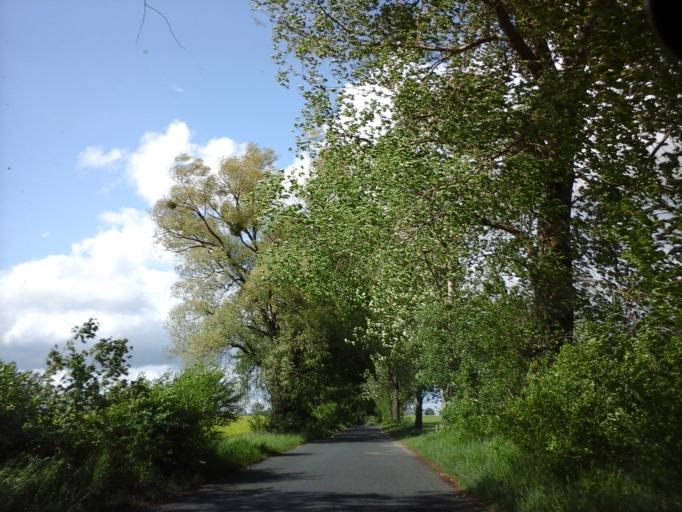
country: PL
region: West Pomeranian Voivodeship
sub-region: Powiat choszczenski
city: Choszczno
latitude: 53.1164
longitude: 15.3991
